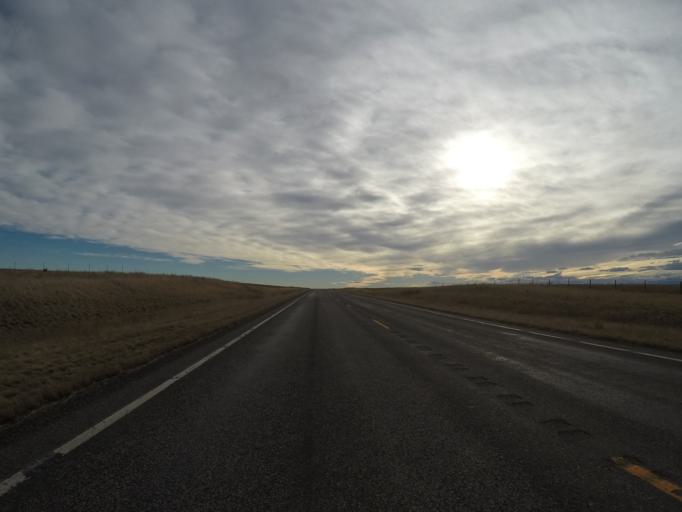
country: US
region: Montana
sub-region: Yellowstone County
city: Laurel
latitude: 45.8403
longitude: -108.8812
